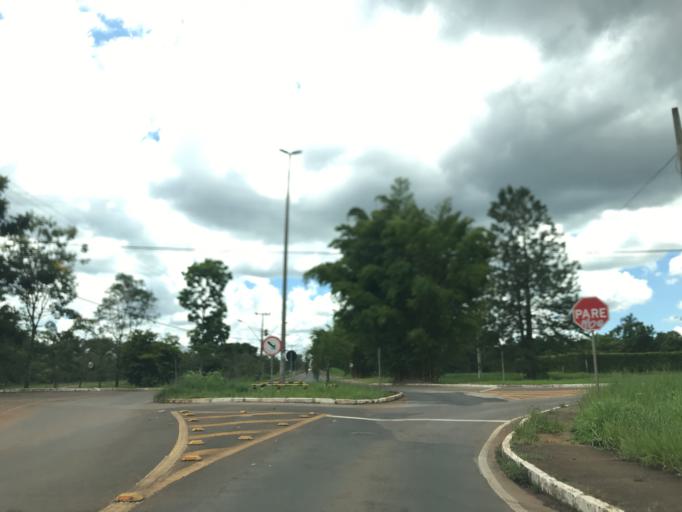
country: BR
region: Federal District
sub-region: Brasilia
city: Brasilia
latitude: -15.8967
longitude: -47.9384
